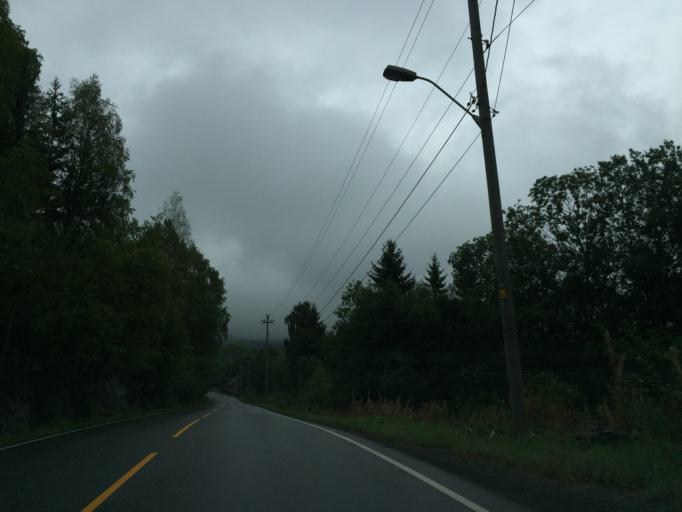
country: NO
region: Akershus
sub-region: Baerum
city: Lysaker
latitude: 60.0100
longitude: 10.6150
